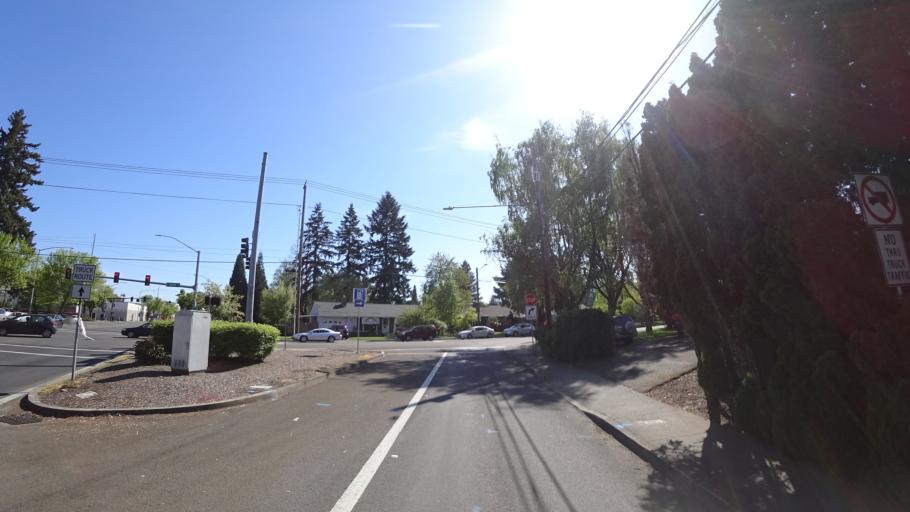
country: US
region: Oregon
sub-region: Washington County
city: Hillsboro
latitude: 45.5224
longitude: -122.9740
